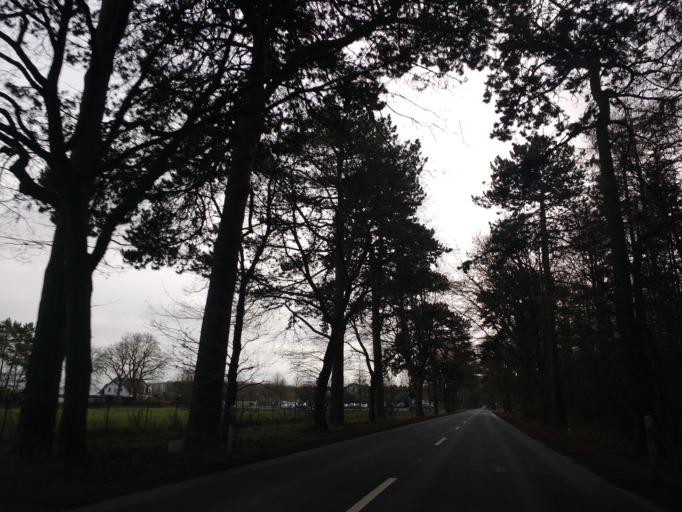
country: DE
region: Schleswig-Holstein
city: Scharbeutz
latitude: 54.0061
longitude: 10.6955
